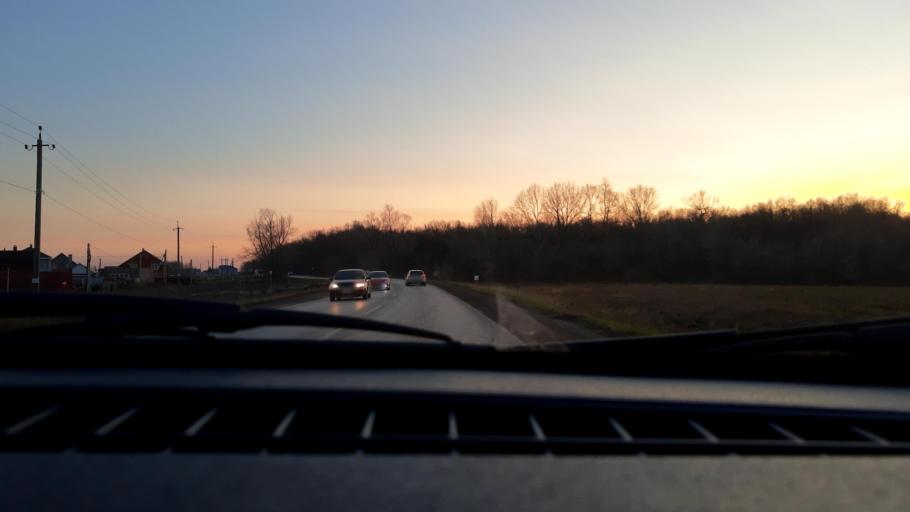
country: RU
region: Bashkortostan
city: Mikhaylovka
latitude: 54.8274
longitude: 55.8837
